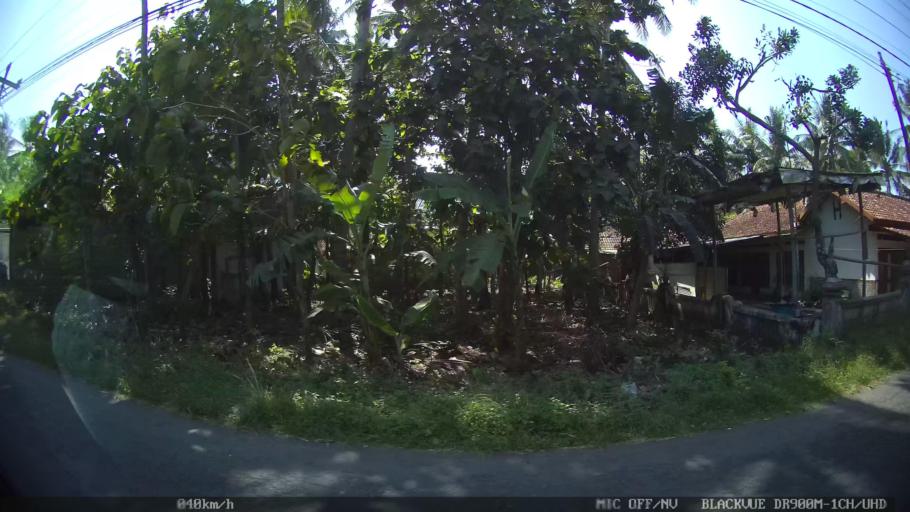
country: ID
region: Daerah Istimewa Yogyakarta
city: Srandakan
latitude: -7.9121
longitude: 110.1538
